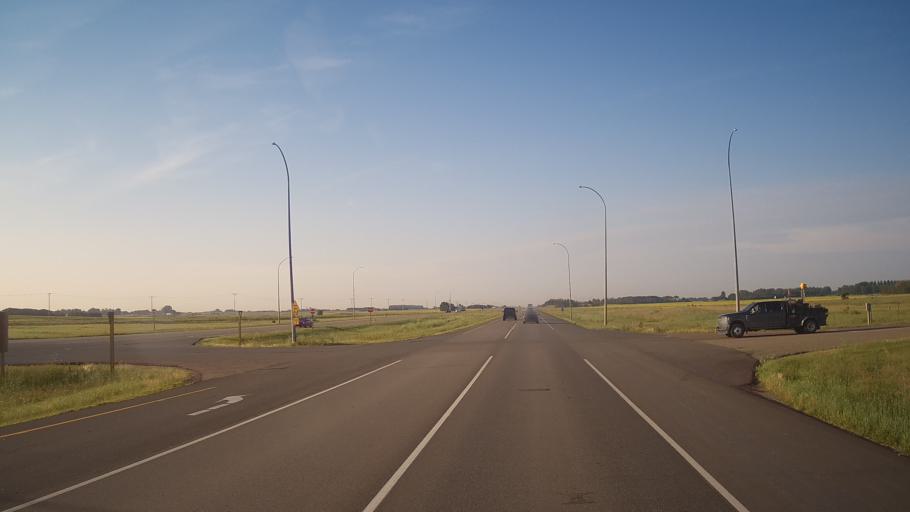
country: CA
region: Saskatchewan
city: Saskatoon
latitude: 52.0542
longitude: -106.5979
